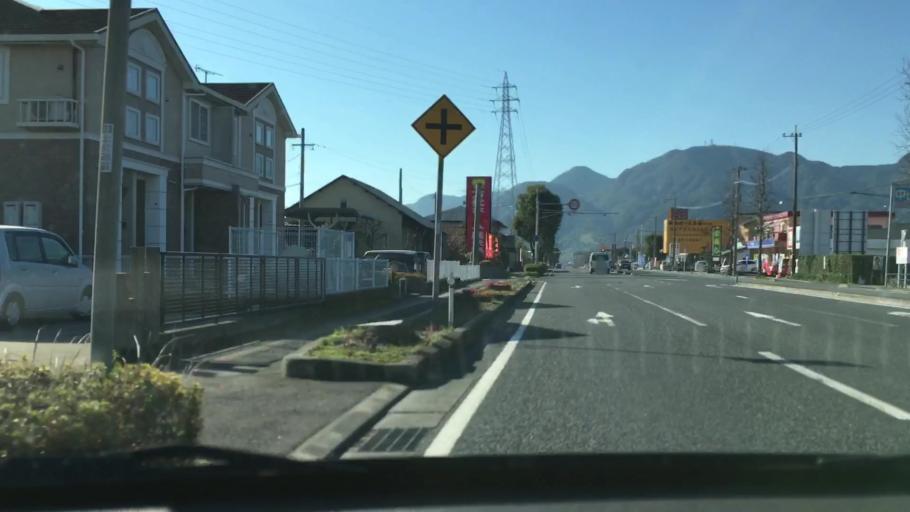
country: JP
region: Kagoshima
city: Kajiki
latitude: 31.7249
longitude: 130.6235
